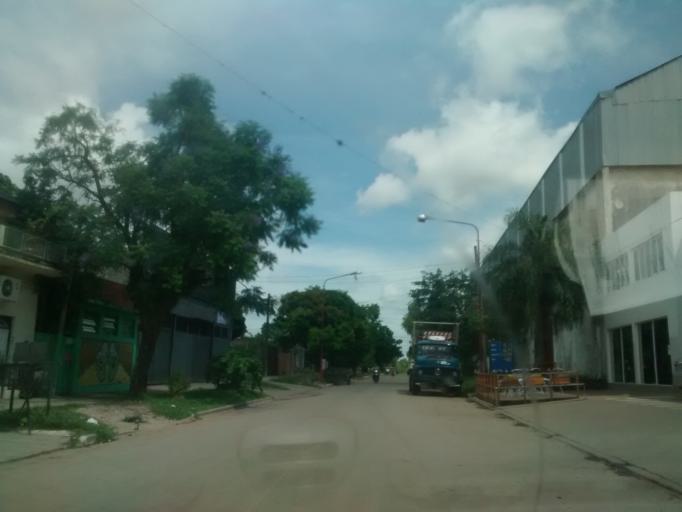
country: AR
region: Chaco
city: Resistencia
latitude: -27.4370
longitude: -58.9852
